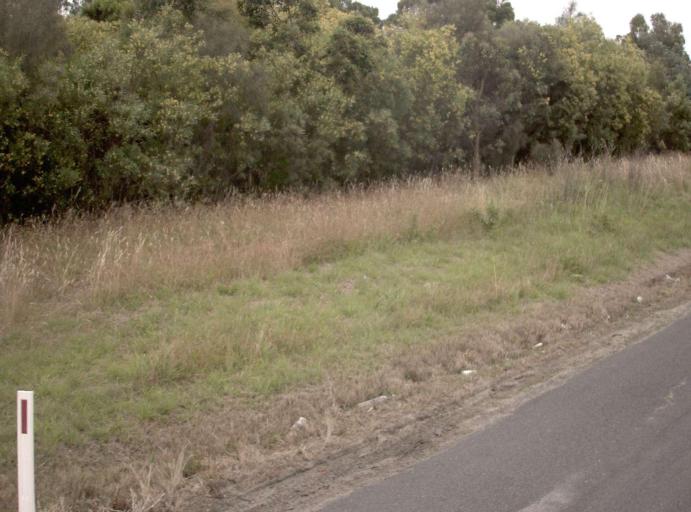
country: AU
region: Victoria
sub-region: Latrobe
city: Traralgon
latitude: -38.2086
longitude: 146.4972
